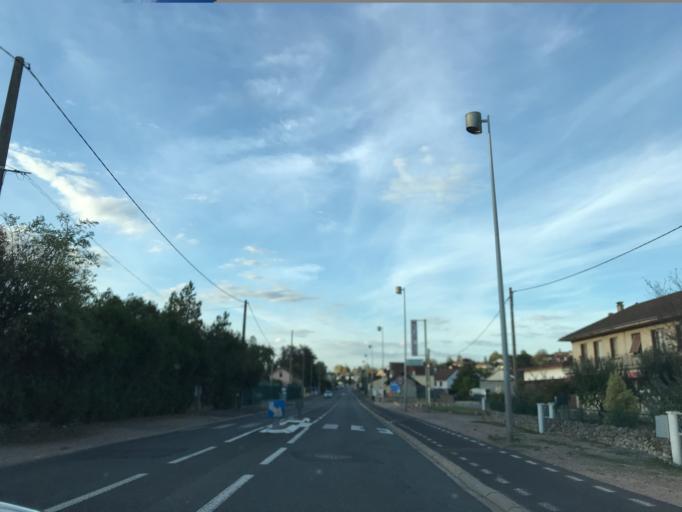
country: FR
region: Auvergne
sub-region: Departement de l'Allier
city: Saint-Yorre
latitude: 46.0575
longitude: 3.4681
